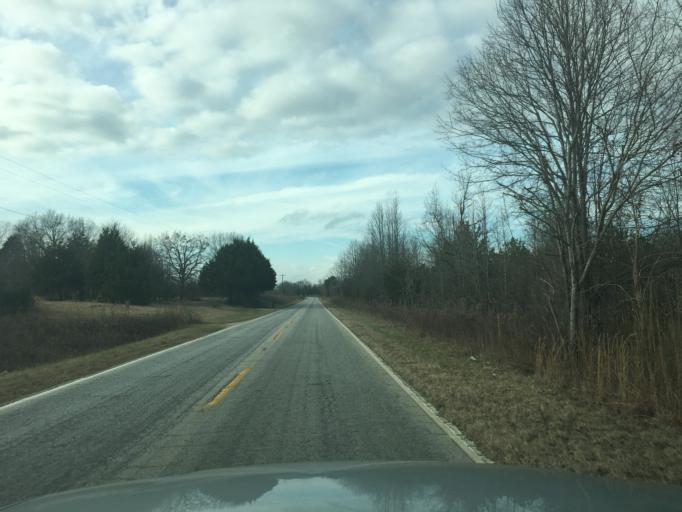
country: US
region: South Carolina
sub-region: Abbeville County
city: Lake Secession
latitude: 34.3539
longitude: -82.5048
